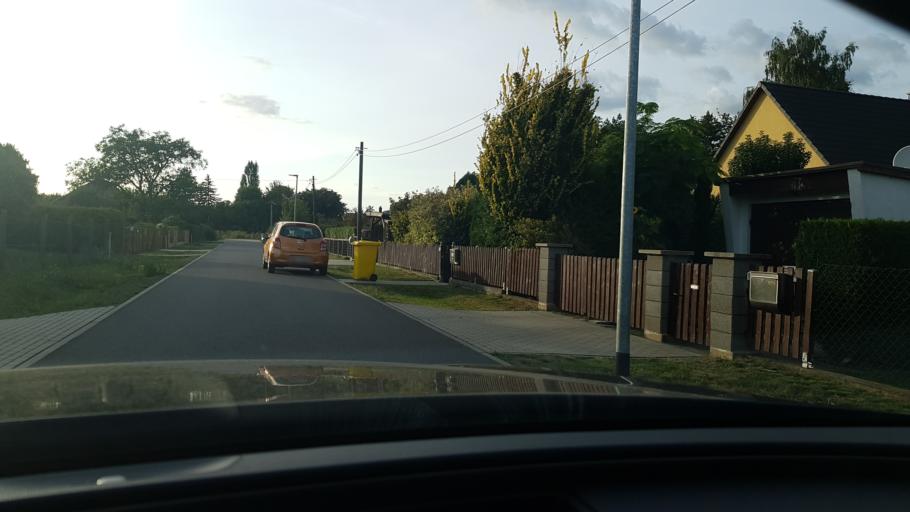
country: DE
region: Brandenburg
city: Brieselang
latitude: 52.5953
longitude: 12.9938
